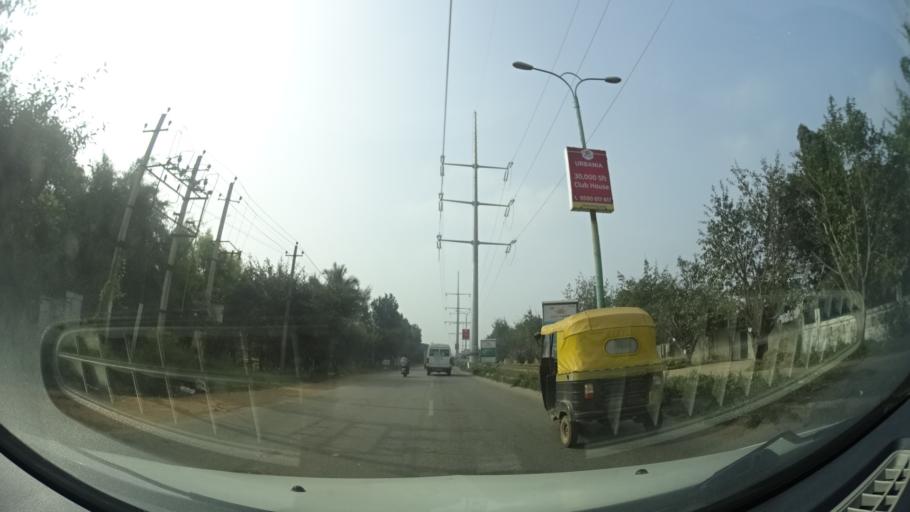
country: IN
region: Karnataka
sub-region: Bangalore Urban
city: Anekal
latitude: 12.7977
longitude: 77.6608
